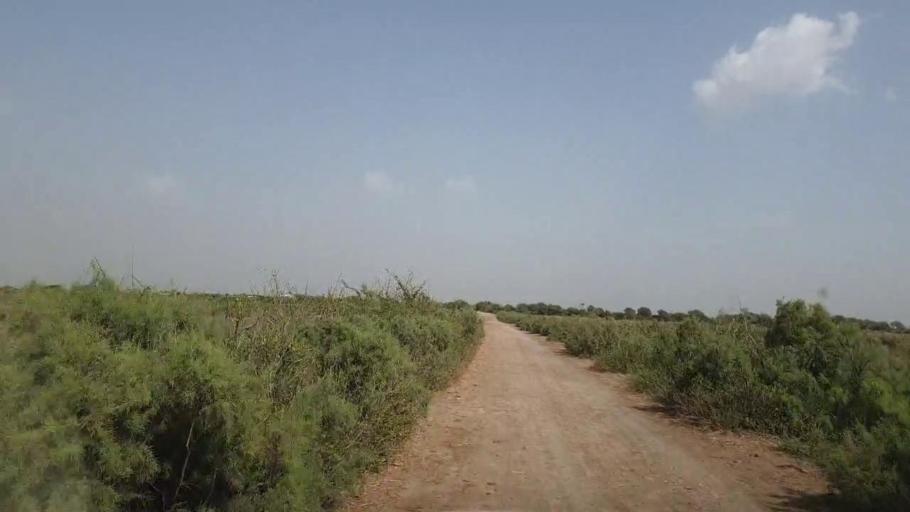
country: PK
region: Sindh
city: Rajo Khanani
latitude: 25.0326
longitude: 68.8778
